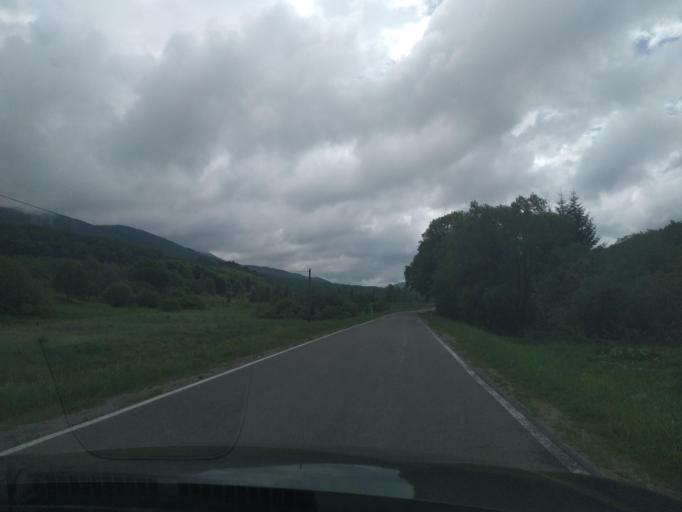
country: PL
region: Subcarpathian Voivodeship
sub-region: Powiat bieszczadzki
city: Lutowiska
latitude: 49.0811
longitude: 22.6552
